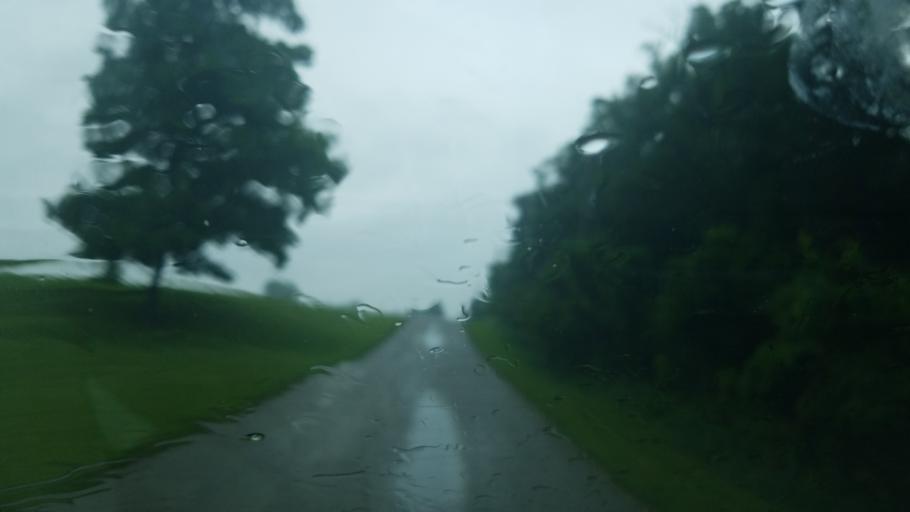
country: US
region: Ohio
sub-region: Richland County
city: Shelby
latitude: 40.9277
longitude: -82.7976
